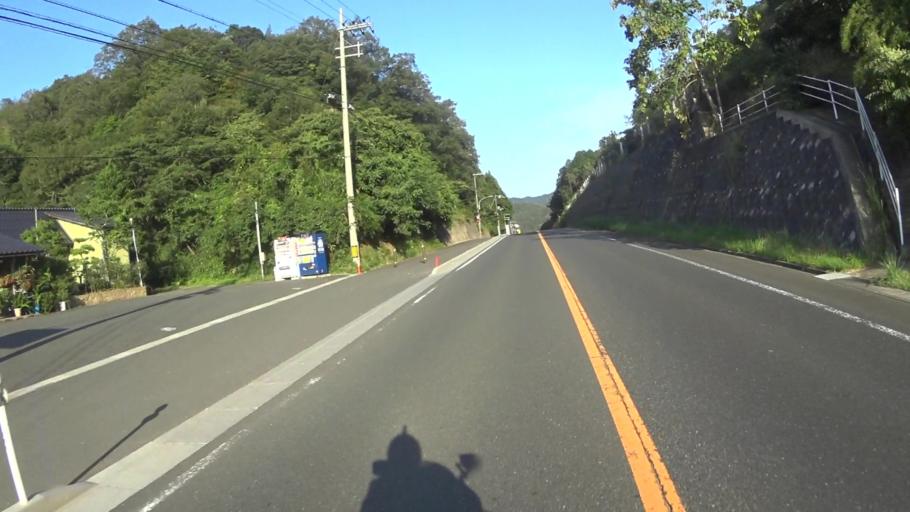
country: JP
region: Hyogo
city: Toyooka
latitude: 35.5837
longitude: 134.9546
